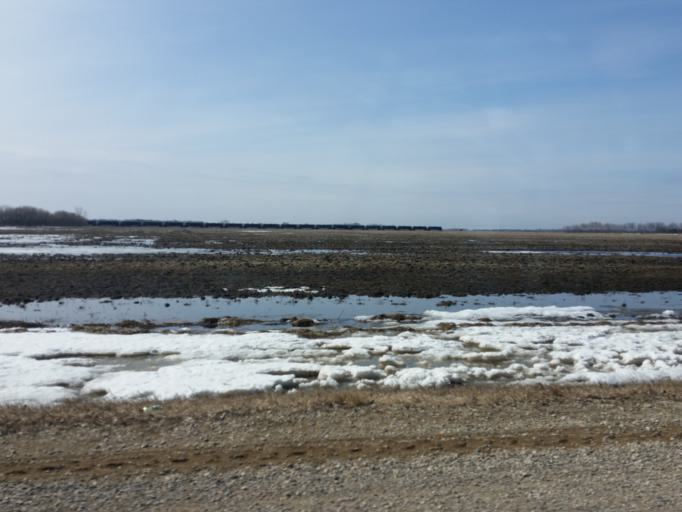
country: US
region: North Dakota
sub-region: Walsh County
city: Grafton
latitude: 48.4345
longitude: -97.4055
